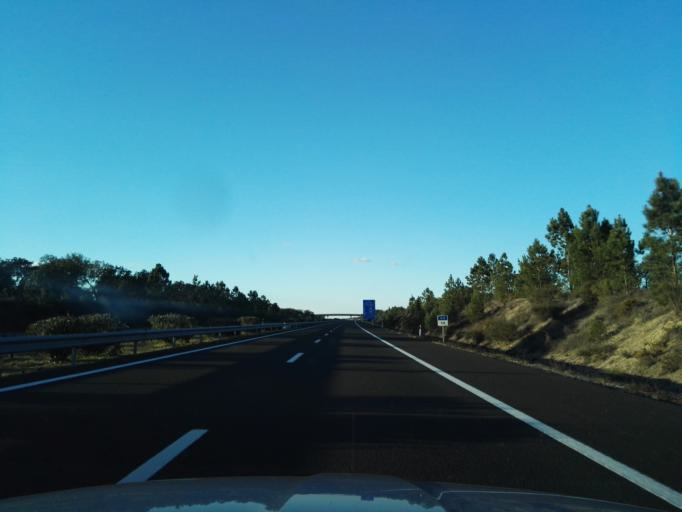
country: PT
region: Santarem
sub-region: Benavente
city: Poceirao
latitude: 38.8234
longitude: -8.7148
